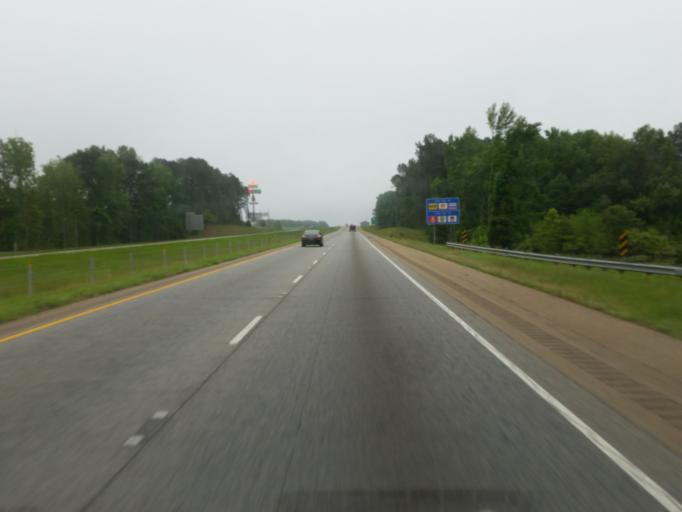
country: US
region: Louisiana
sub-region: Webster Parish
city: Minden
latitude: 32.5822
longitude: -93.2570
